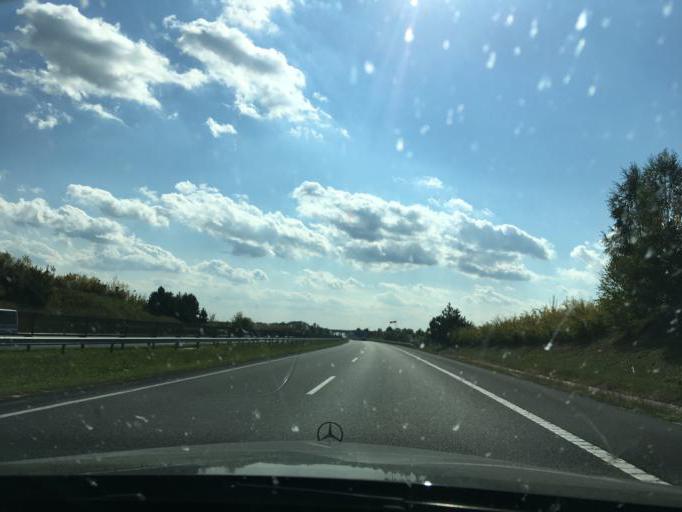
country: HU
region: Zala
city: Nagykanizsa
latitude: 46.4733
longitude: 16.9001
